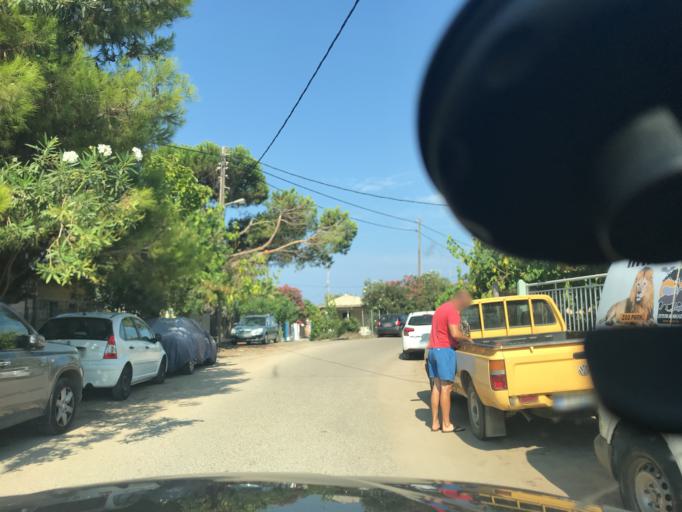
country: GR
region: West Greece
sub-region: Nomos Ileias
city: Kardamas
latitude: 37.7197
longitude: 21.3124
